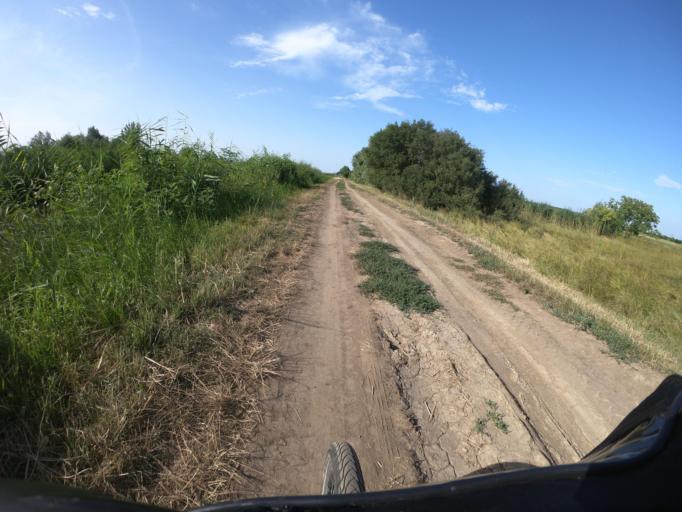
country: HU
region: Hajdu-Bihar
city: Tiszacsege
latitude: 47.6053
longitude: 20.9965
